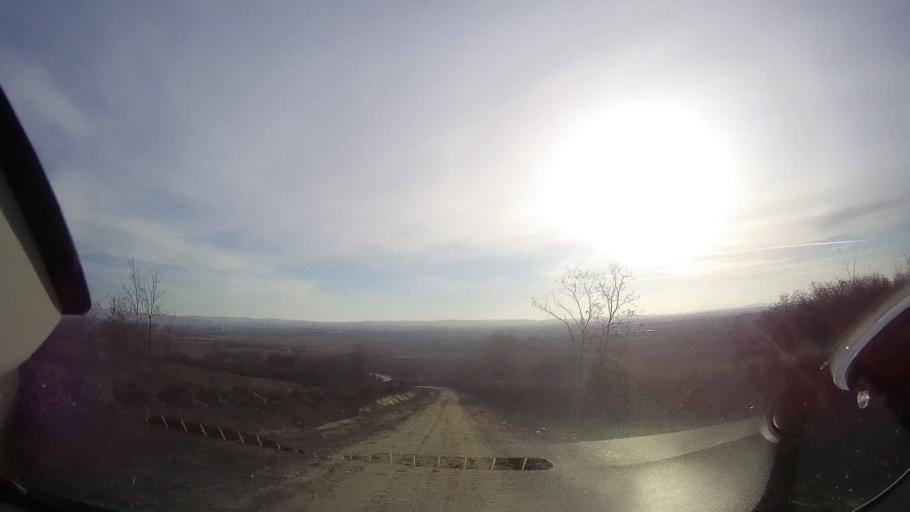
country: RO
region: Bihor
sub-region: Comuna Tileagd
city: Tileagd
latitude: 47.0966
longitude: 22.1776
